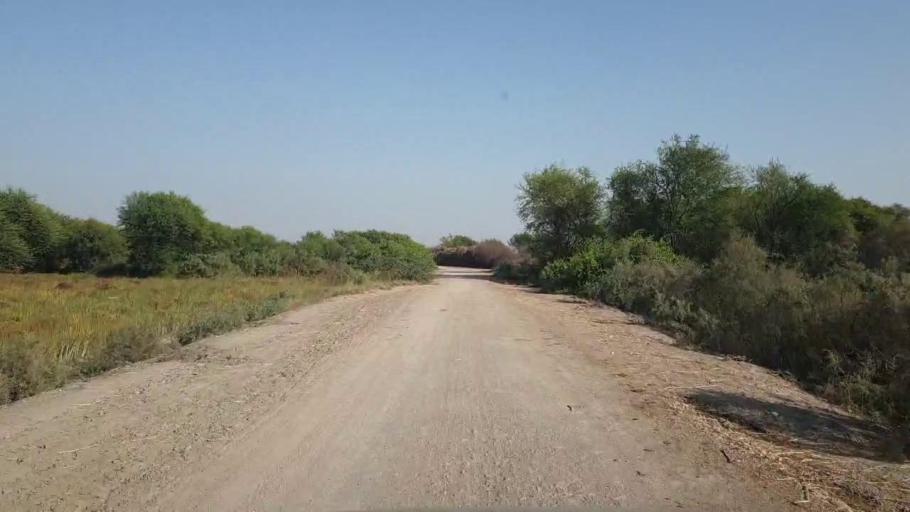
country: PK
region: Sindh
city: Rajo Khanani
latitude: 25.0084
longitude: 68.7707
